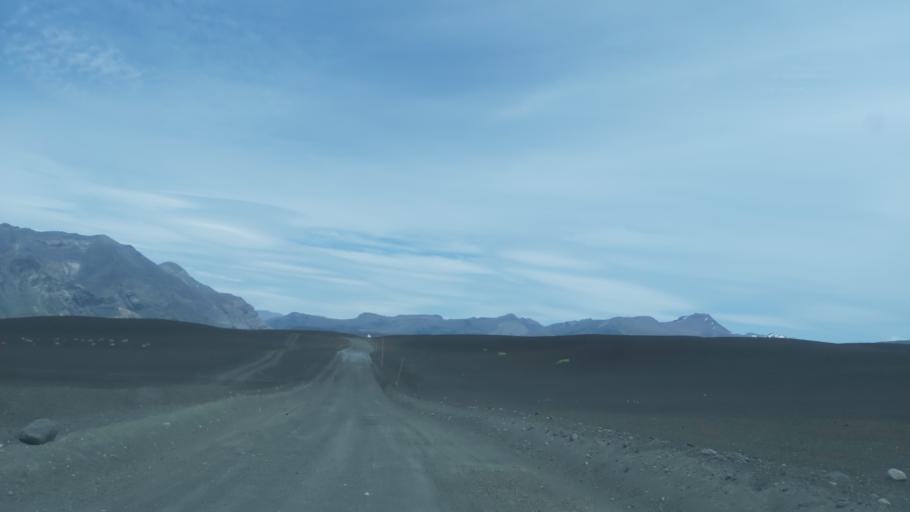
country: AR
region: Neuquen
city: Andacollo
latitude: -37.4320
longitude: -71.2858
